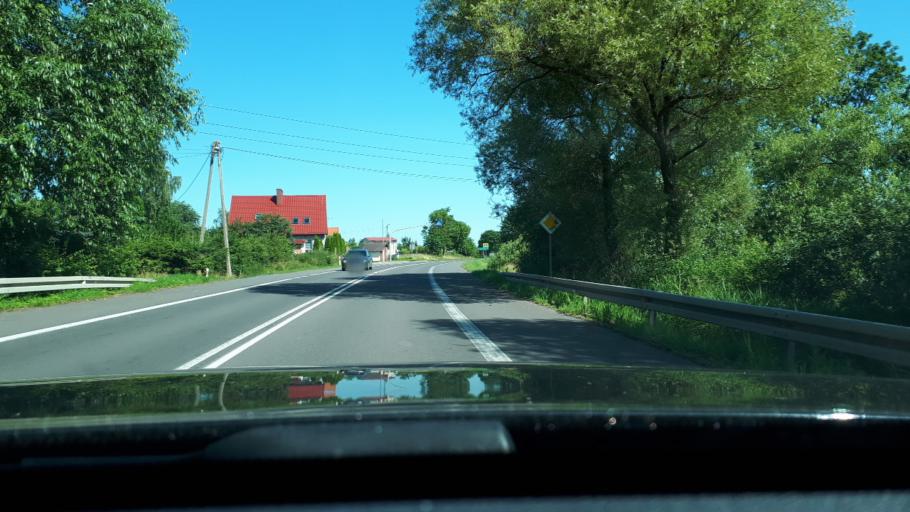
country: PL
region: Warmian-Masurian Voivodeship
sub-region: Powiat ostrodzki
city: Ostroda
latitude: 53.6464
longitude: 20.0516
